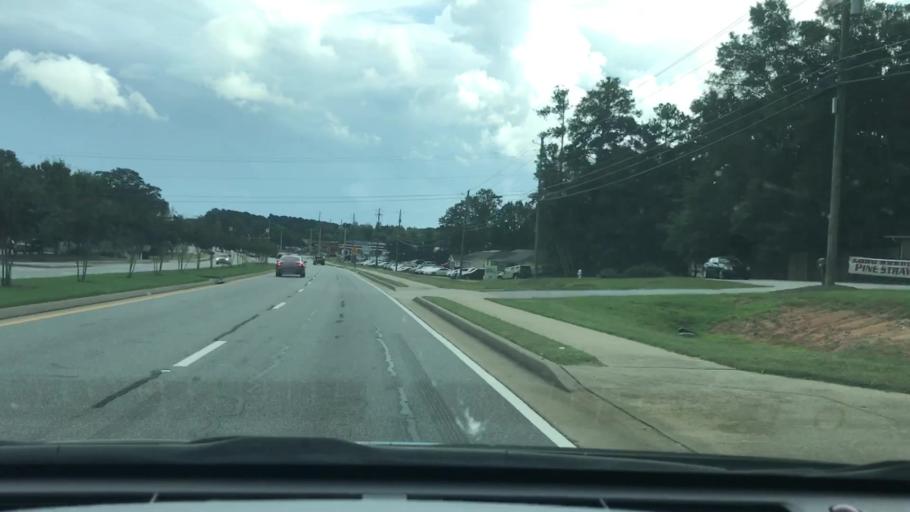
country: US
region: Georgia
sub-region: Gwinnett County
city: Grayson
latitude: 33.8832
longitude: -83.9417
